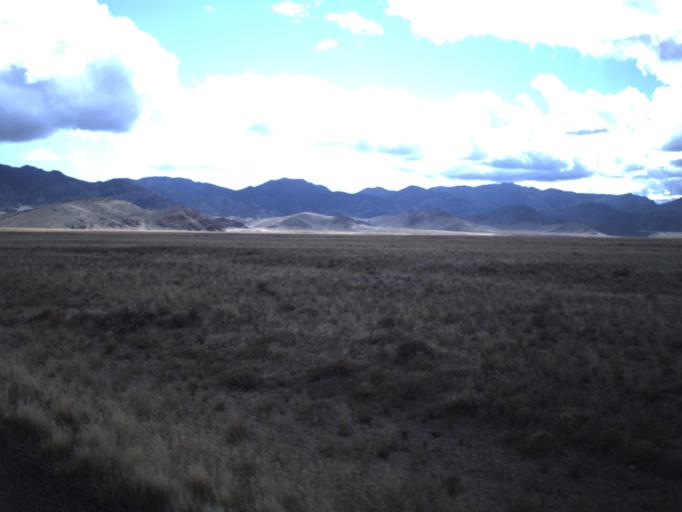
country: US
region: Utah
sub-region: Beaver County
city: Milford
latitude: 38.5157
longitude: -113.6369
